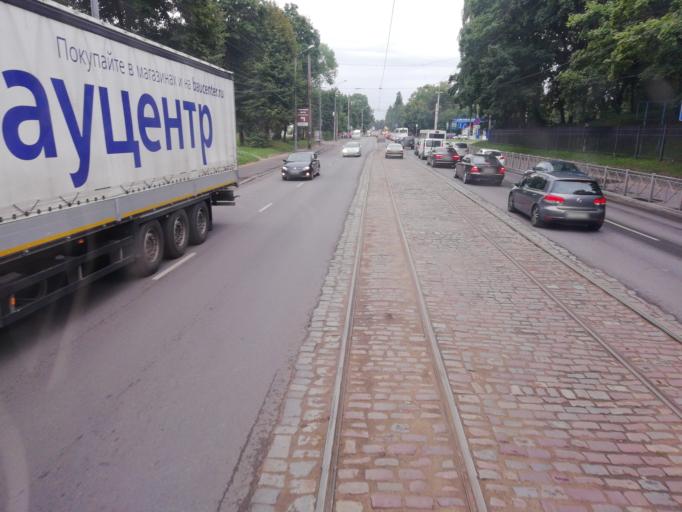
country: RU
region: Kaliningrad
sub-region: Gorod Kaliningrad
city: Kaliningrad
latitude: 54.6949
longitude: 20.5232
